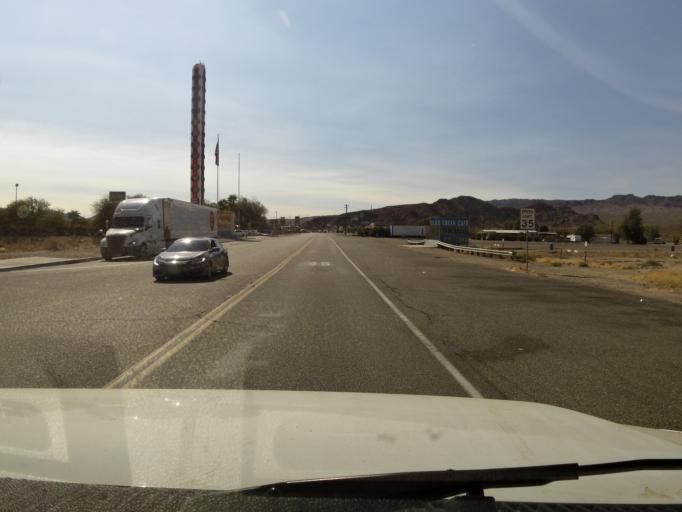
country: US
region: California
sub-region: San Bernardino County
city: Fort Irwin
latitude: 35.2672
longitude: -116.0722
